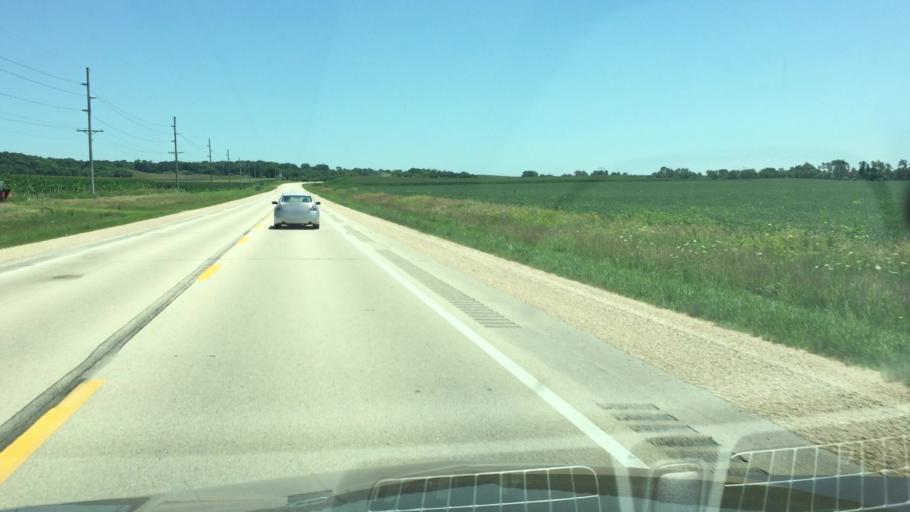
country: US
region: Iowa
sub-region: Jackson County
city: Maquoketa
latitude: 42.0660
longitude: -90.7744
